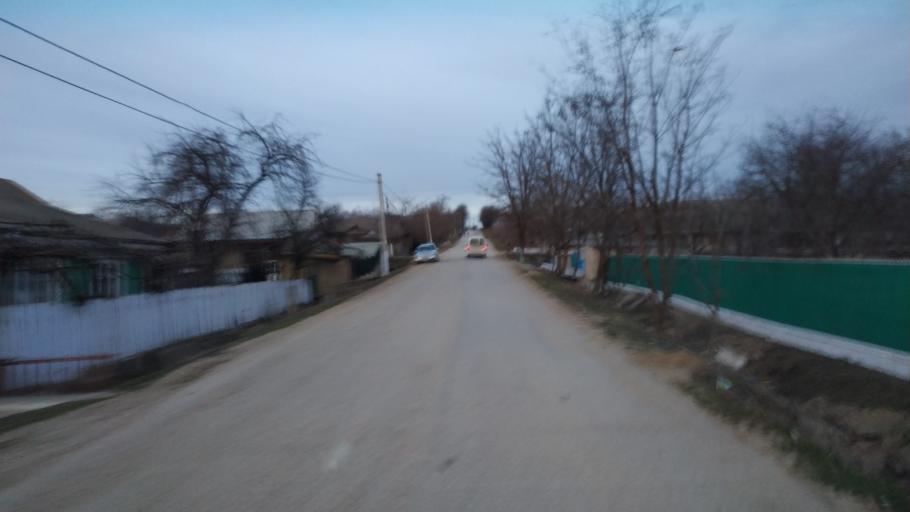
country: MD
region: Hincesti
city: Dancu
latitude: 46.7391
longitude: 28.2149
